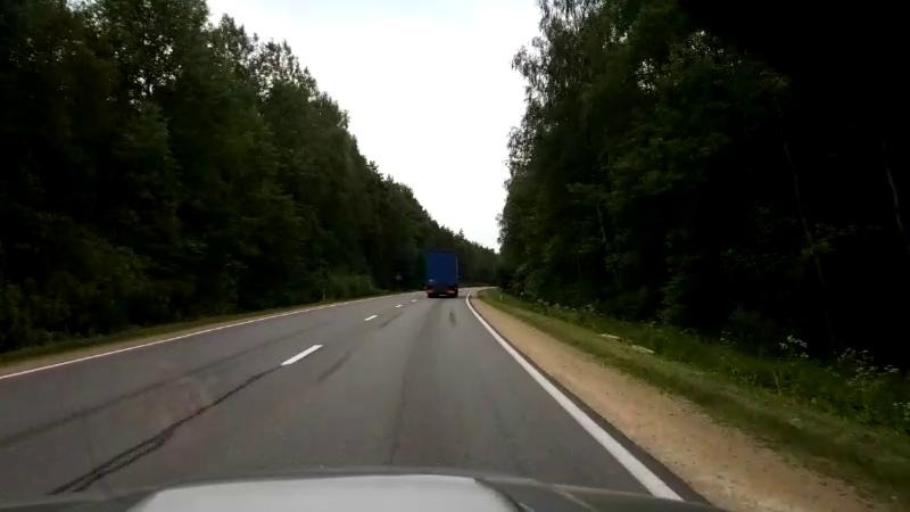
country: LV
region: Salaspils
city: Salaspils
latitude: 56.9079
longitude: 24.4058
